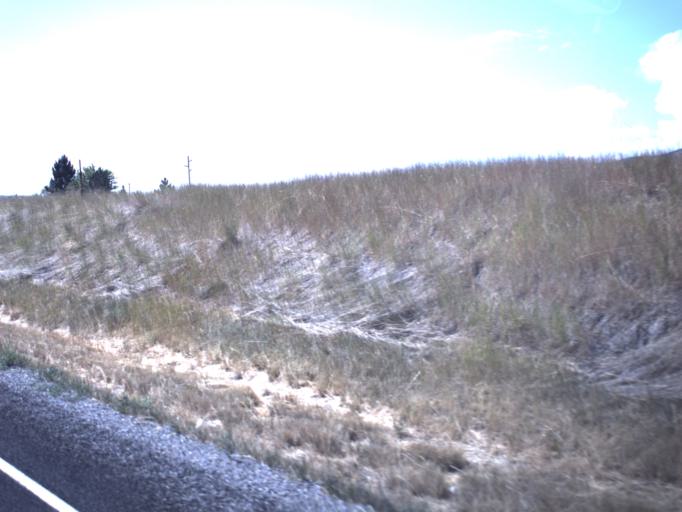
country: US
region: Utah
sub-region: Box Elder County
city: Garland
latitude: 41.8302
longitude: -112.1458
